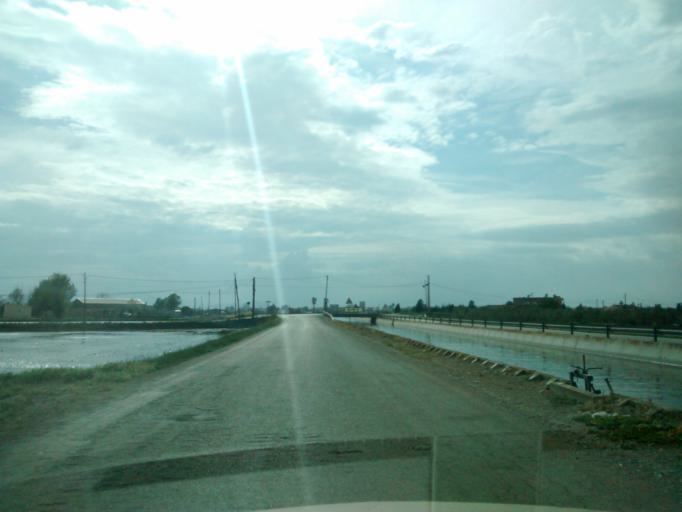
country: ES
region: Catalonia
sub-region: Provincia de Tarragona
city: Deltebre
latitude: 40.7023
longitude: 0.7317
